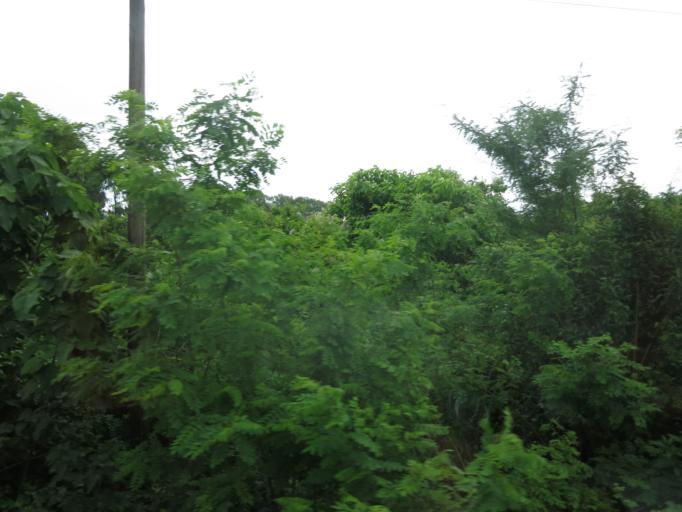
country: GE
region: Imereti
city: Samtredia
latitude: 42.1284
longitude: 42.3337
